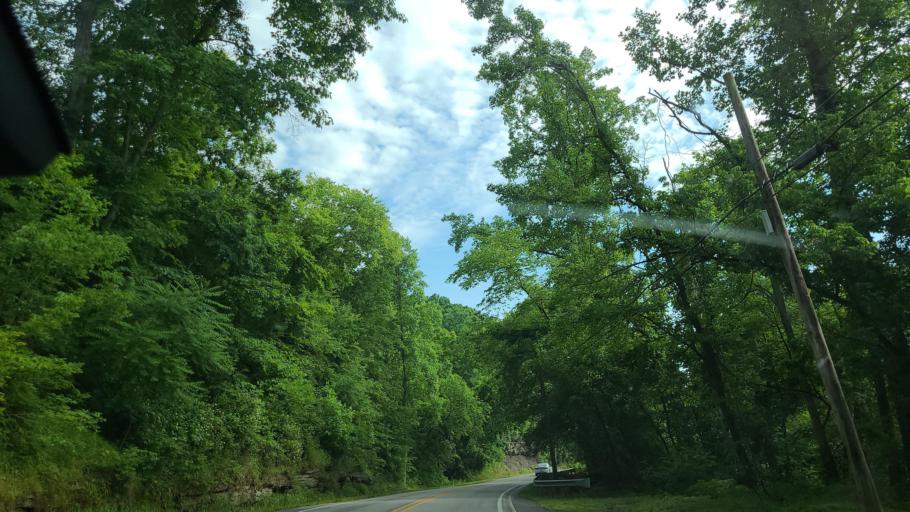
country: US
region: Kentucky
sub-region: Whitley County
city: Williamsburg
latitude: 36.7371
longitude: -84.1067
